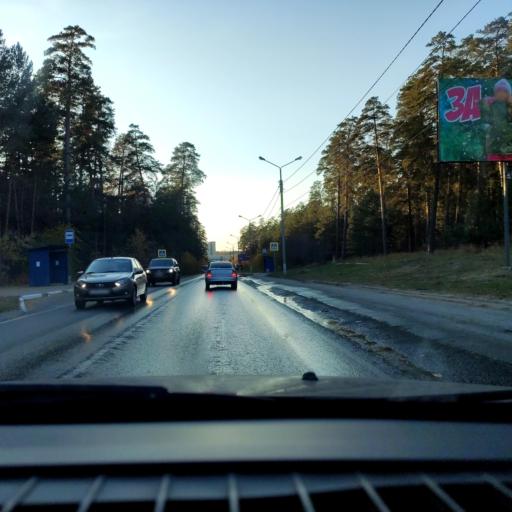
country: RU
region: Samara
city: Tol'yatti
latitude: 53.4760
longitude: 49.3334
